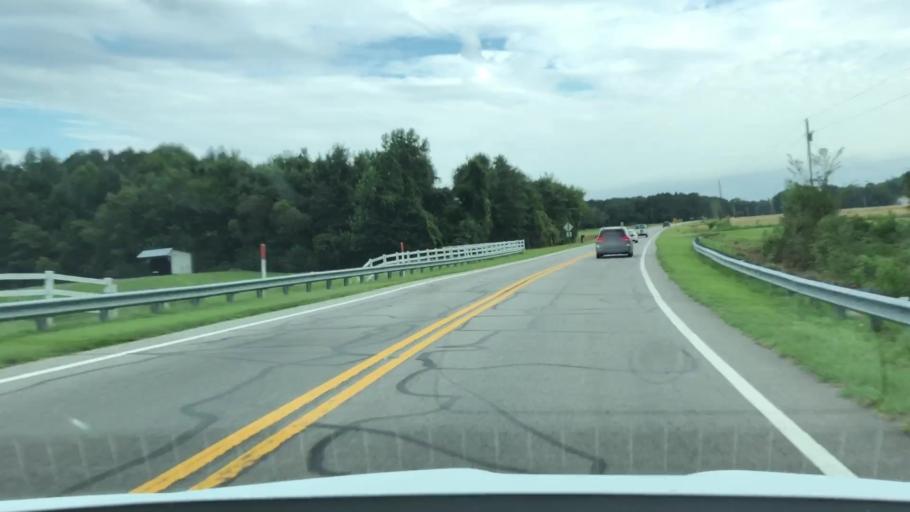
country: US
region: North Carolina
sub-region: Lenoir County
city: Kinston
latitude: 35.1579
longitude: -77.5537
